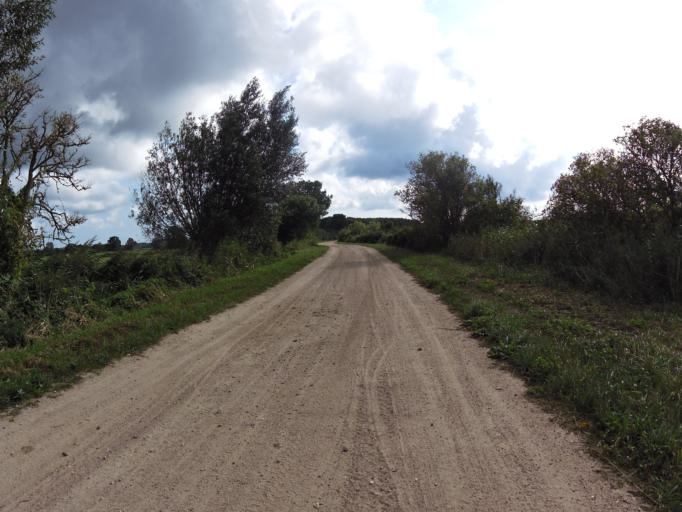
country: DE
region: Mecklenburg-Vorpommern
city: Loddin
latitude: 53.9903
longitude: 14.0575
